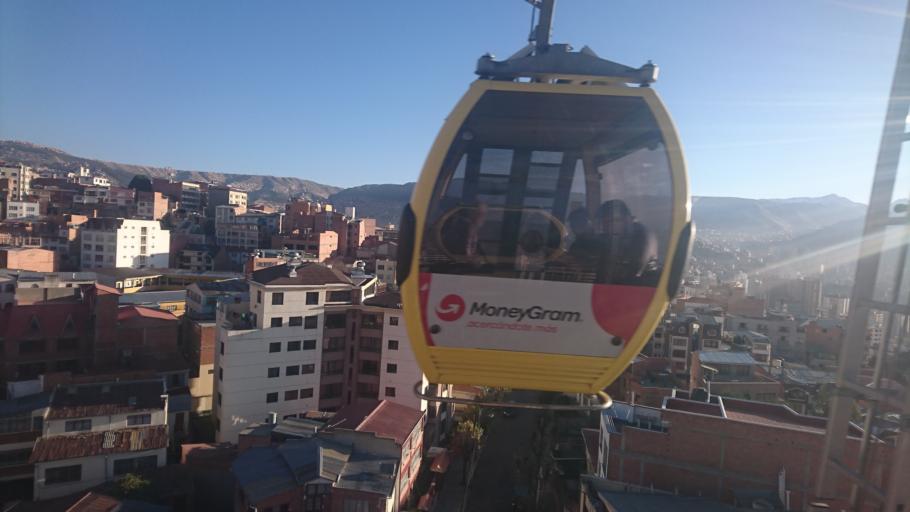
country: BO
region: La Paz
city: La Paz
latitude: -16.5149
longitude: -68.1342
